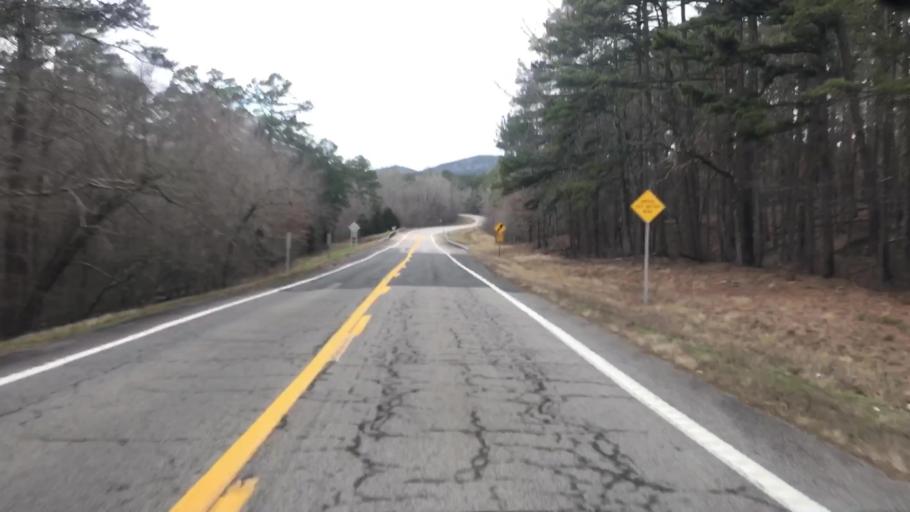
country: US
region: Arkansas
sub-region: Montgomery County
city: Mount Ida
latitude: 34.6847
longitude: -93.8033
